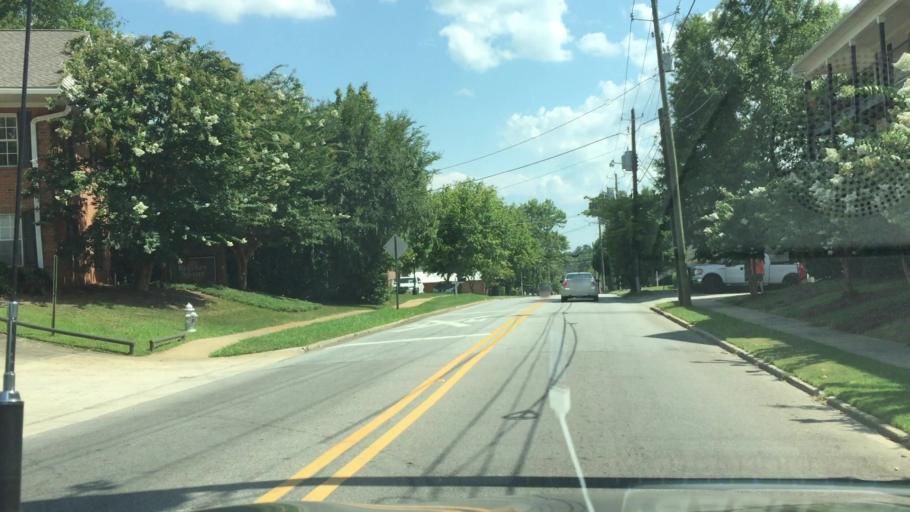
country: US
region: Alabama
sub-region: Lee County
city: Auburn
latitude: 32.6117
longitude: -85.4754
